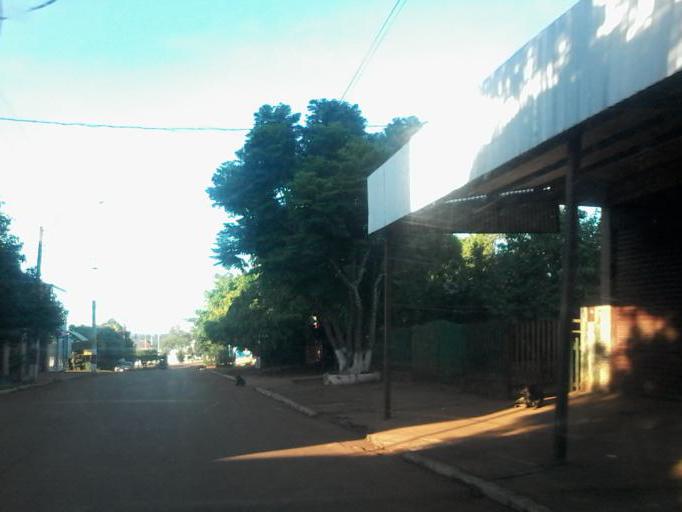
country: PY
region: Alto Parana
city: Ciudad del Este
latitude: -25.4371
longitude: -54.6426
